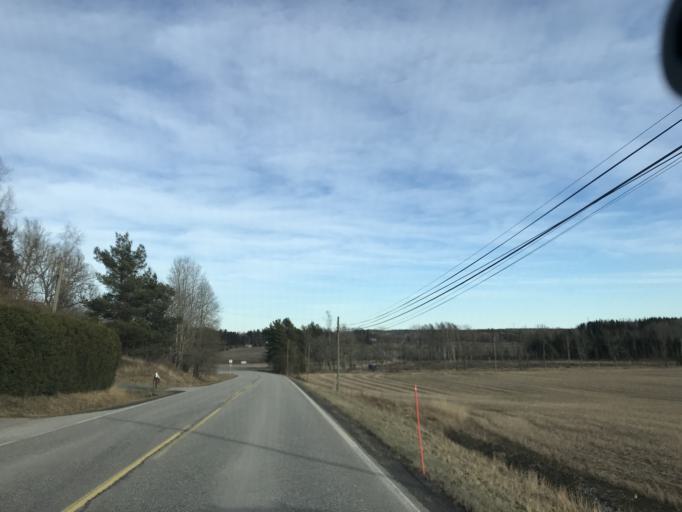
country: FI
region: Uusimaa
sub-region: Raaseporin
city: Pohja
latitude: 60.0907
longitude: 23.4894
